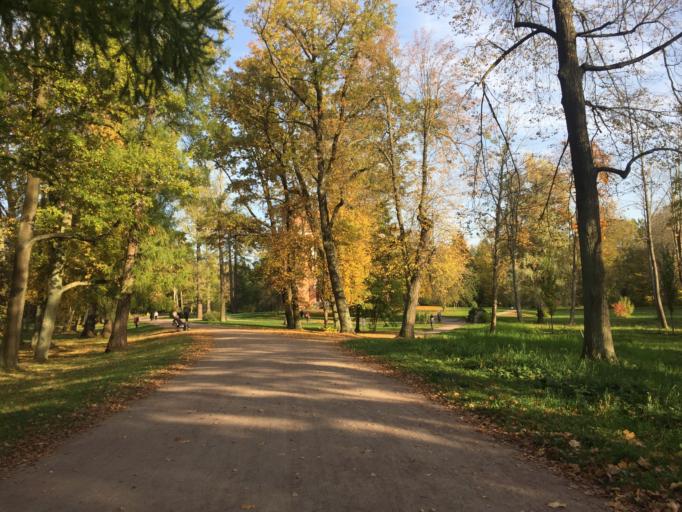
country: RU
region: St.-Petersburg
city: Pushkin
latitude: 59.7220
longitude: 30.3750
